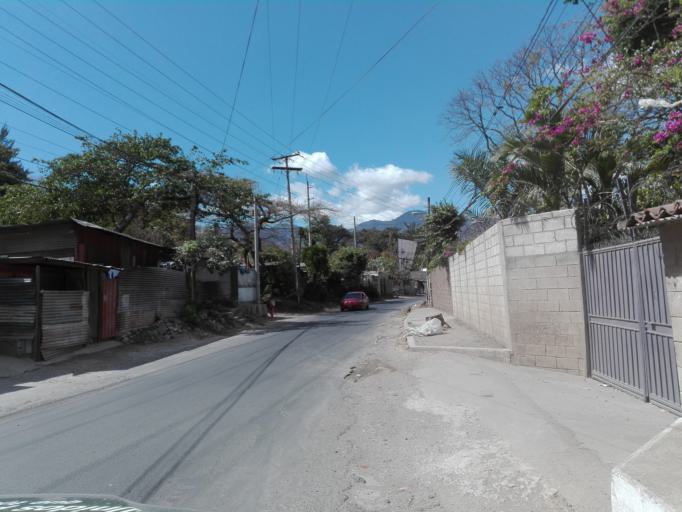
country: GT
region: Guatemala
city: Amatitlan
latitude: 14.4720
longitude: -90.6061
